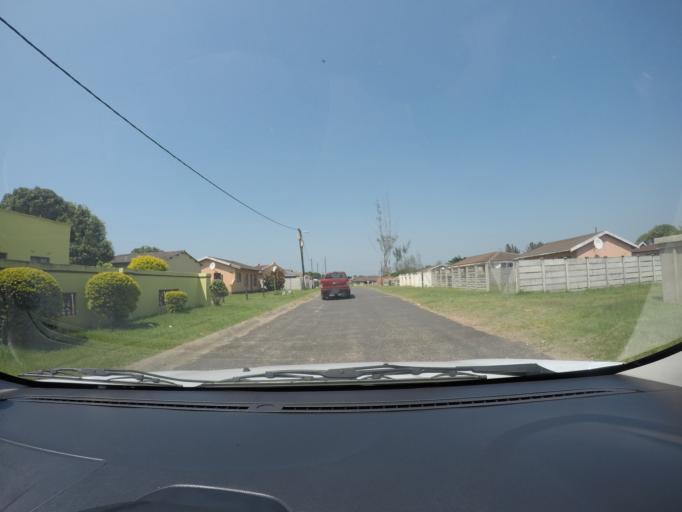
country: ZA
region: KwaZulu-Natal
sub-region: uThungulu District Municipality
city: eSikhawini
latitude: -28.8630
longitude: 31.9208
